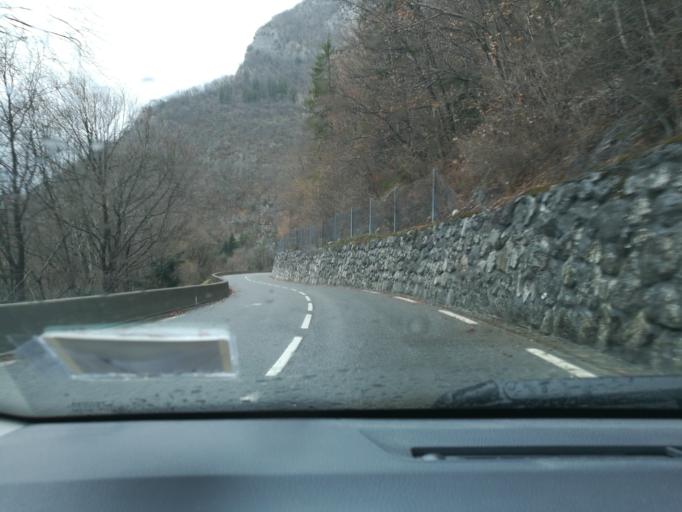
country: FR
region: Rhone-Alpes
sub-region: Departement de la Haute-Savoie
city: Araches-la-Frasse
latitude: 46.0437
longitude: 6.6146
